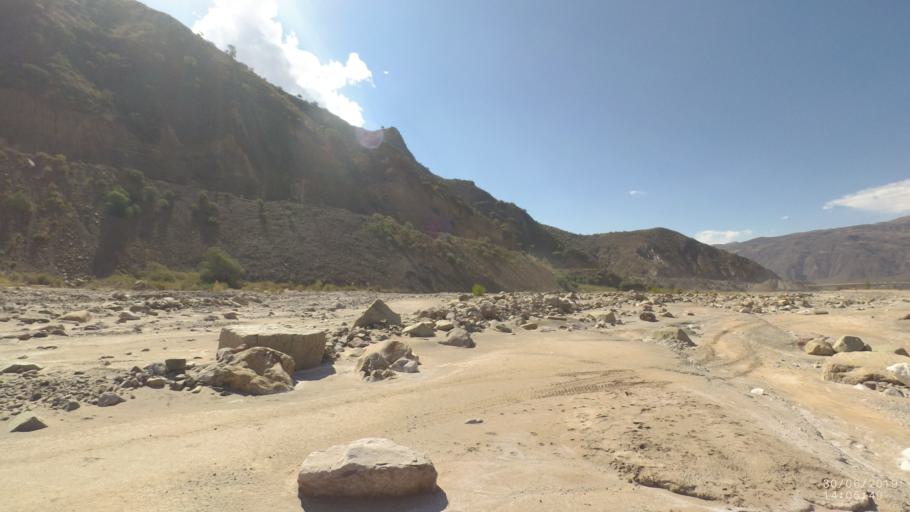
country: BO
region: Cochabamba
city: Irpa Irpa
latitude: -17.8046
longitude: -66.3571
